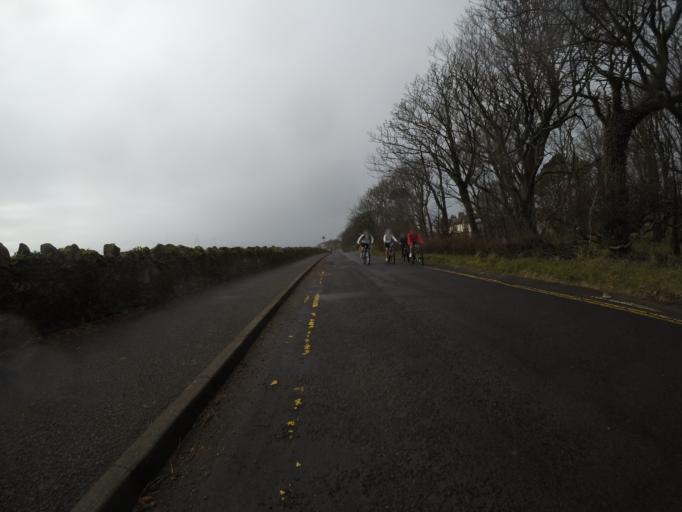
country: GB
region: Scotland
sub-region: North Ayrshire
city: West Kilbride
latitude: 55.6958
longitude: -4.8745
